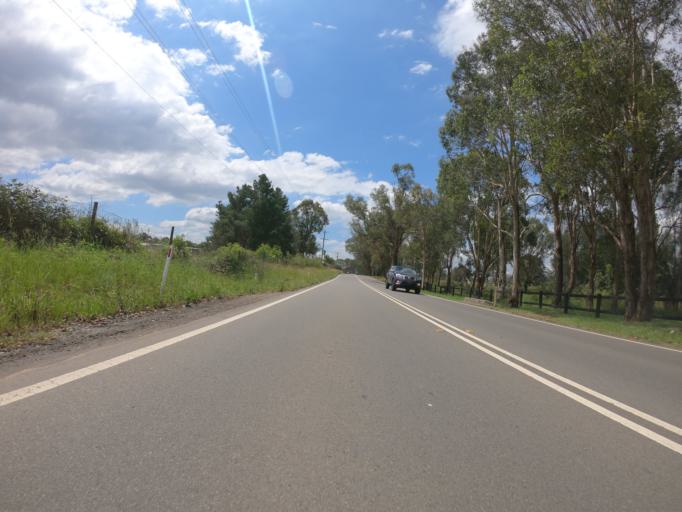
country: AU
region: New South Wales
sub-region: Penrith Municipality
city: Kingswood Park
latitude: -33.8317
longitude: 150.7578
